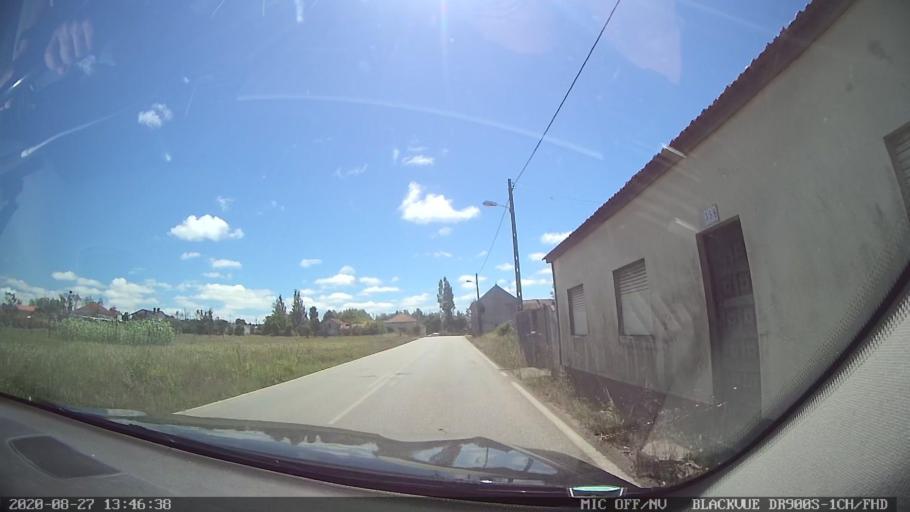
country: PT
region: Coimbra
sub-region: Mira
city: Mira
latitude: 40.3946
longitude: -8.7360
